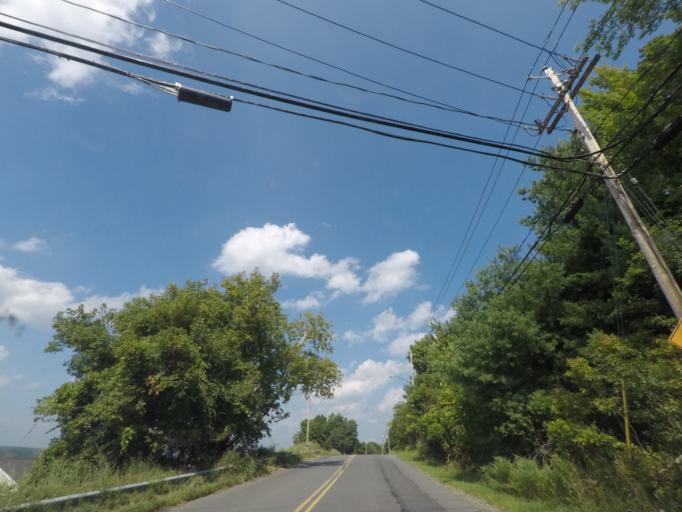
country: US
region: New York
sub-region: Saratoga County
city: Waterford
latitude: 42.7775
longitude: -73.6650
